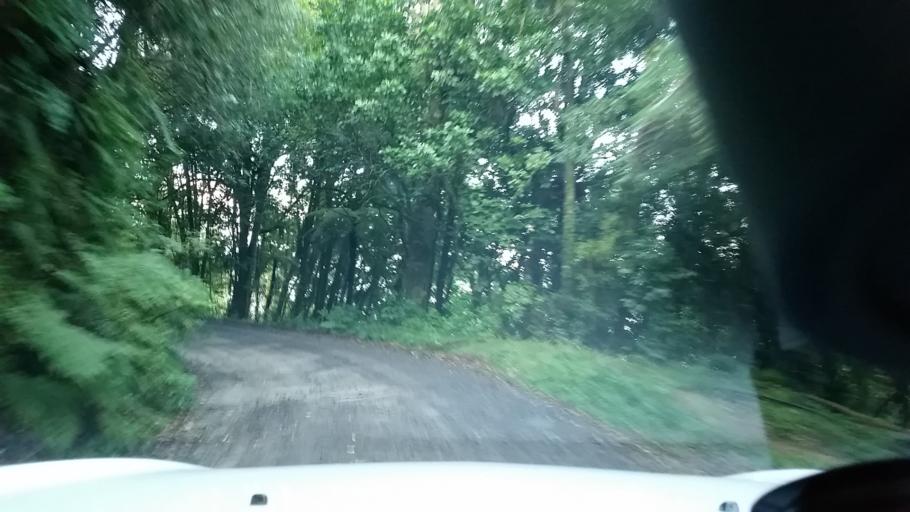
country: NZ
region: Bay of Plenty
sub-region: Kawerau District
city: Kawerau
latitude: -38.0178
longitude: 176.5917
